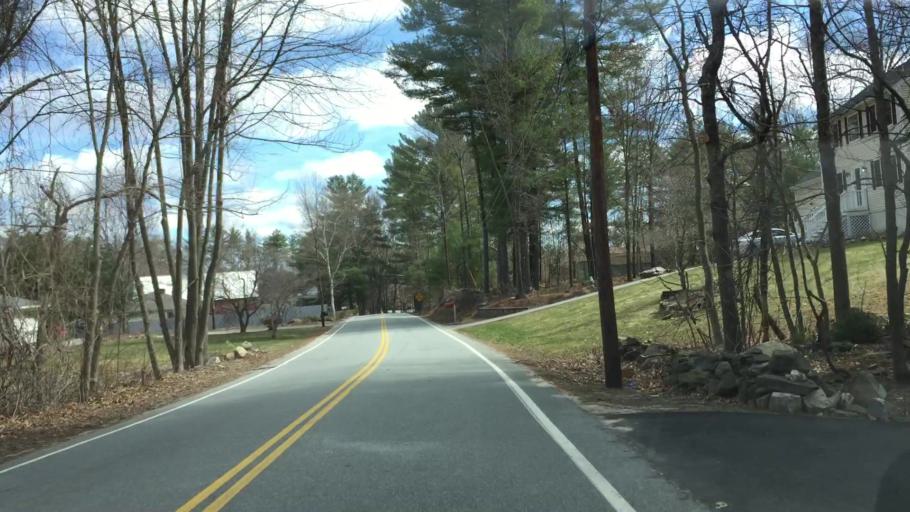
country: US
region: New Hampshire
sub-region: Hillsborough County
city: Pelham
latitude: 42.7146
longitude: -71.3434
